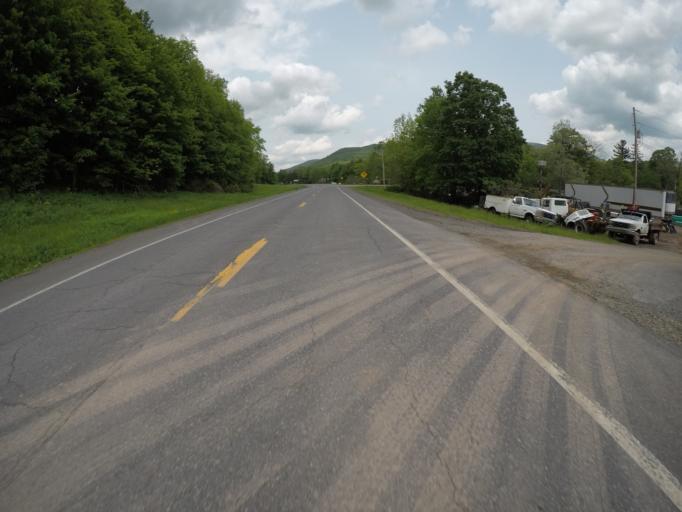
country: US
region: New York
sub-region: Delaware County
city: Stamford
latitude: 42.3006
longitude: -74.5556
